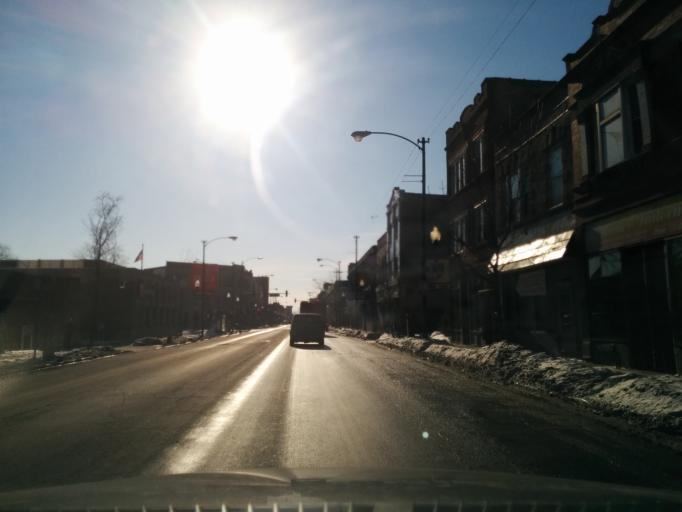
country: US
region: Illinois
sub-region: Cook County
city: Lincolnwood
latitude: 41.9358
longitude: -87.7185
